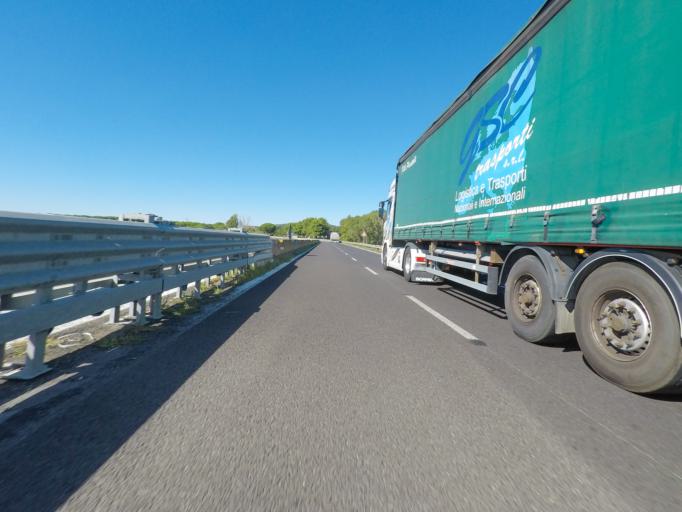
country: IT
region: Latium
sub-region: Provincia di Viterbo
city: Pescia Romana
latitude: 42.4108
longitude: 11.4771
